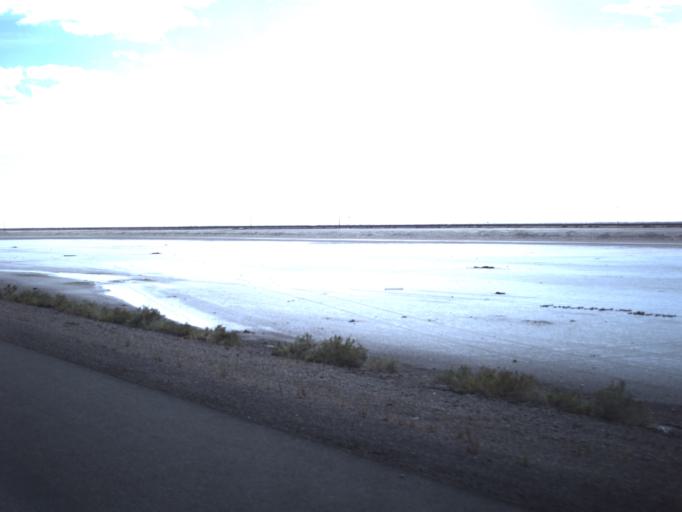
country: US
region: Utah
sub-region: Tooele County
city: Wendover
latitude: 40.7403
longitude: -113.9436
